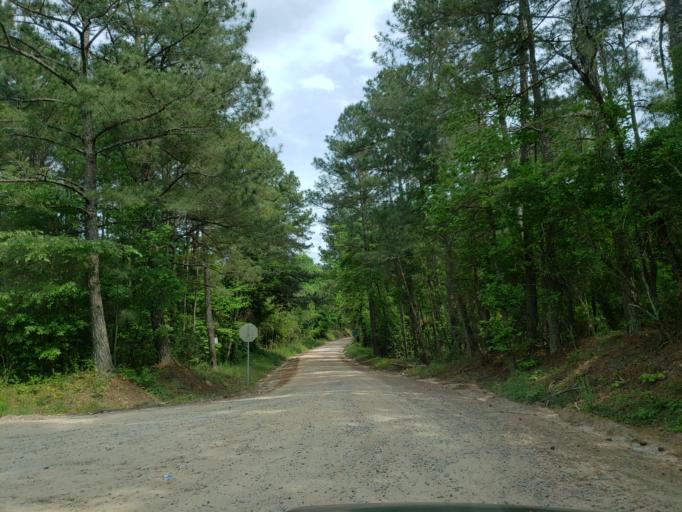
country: US
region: Georgia
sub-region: Monroe County
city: Forsyth
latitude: 32.9873
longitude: -83.9170
